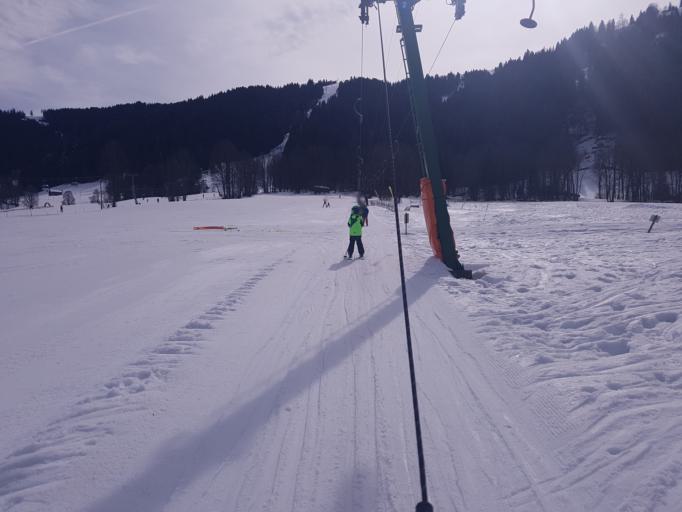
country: AT
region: Tyrol
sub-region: Politischer Bezirk Kufstein
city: Worgl
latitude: 47.4471
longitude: 12.0908
